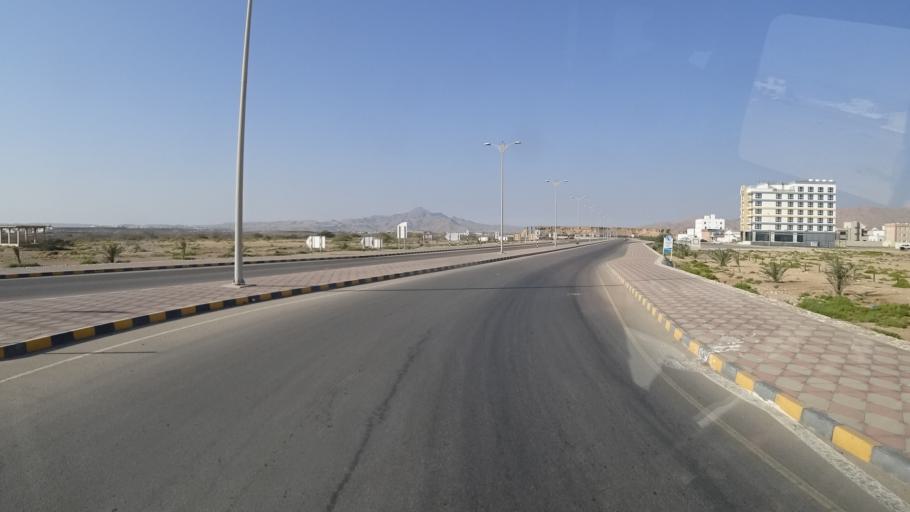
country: OM
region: Ash Sharqiyah
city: Sur
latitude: 22.6026
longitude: 59.4830
